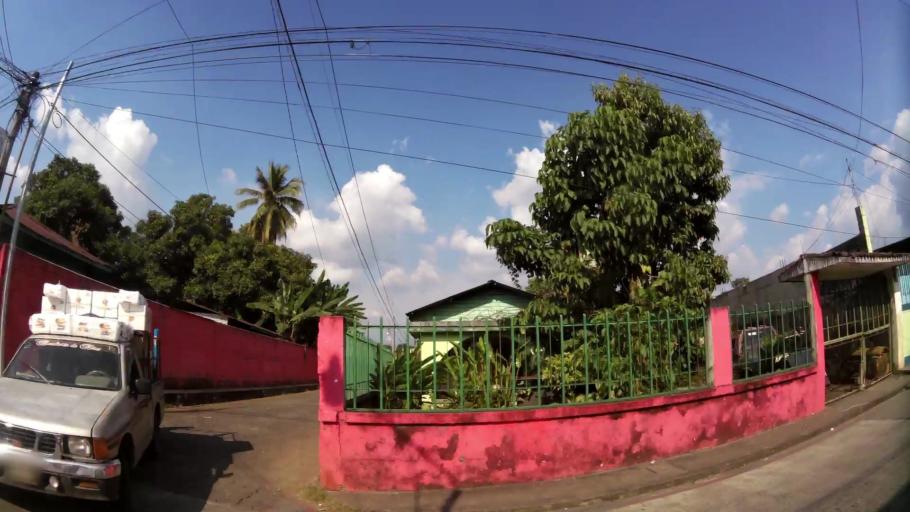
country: GT
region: Retalhuleu
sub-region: Municipio de Retalhuleu
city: Retalhuleu
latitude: 14.5393
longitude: -91.6878
